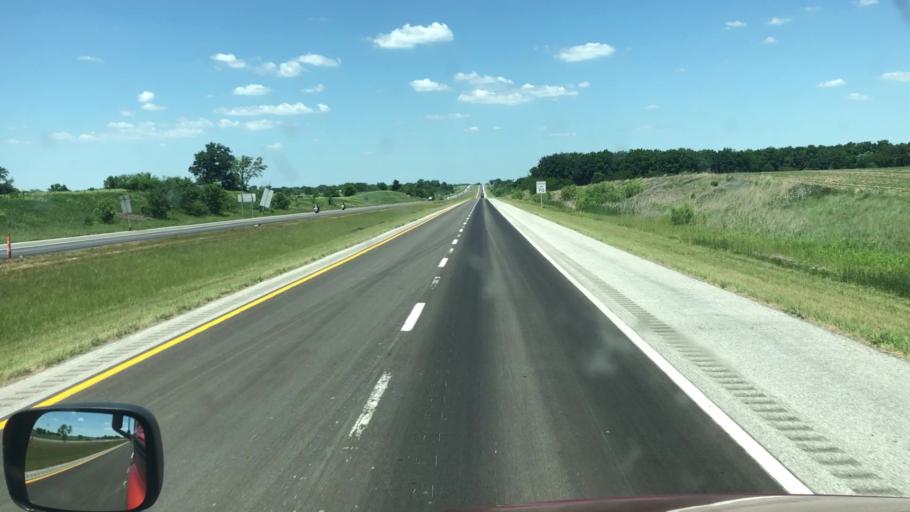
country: US
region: Missouri
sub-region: Macon County
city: La Plata
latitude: 39.9854
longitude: -92.4756
